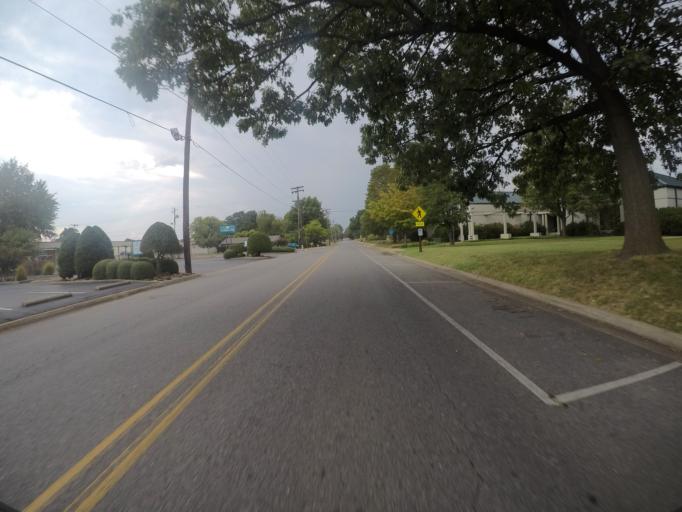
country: US
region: Arkansas
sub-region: Washington County
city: Springdale
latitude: 36.1864
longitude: -94.1315
